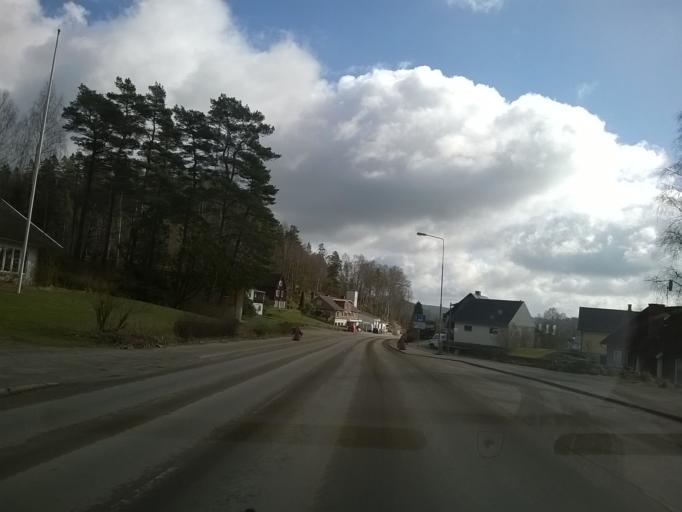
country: SE
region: Halland
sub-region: Falkenbergs Kommun
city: Falkenberg
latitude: 57.1379
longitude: 12.7067
